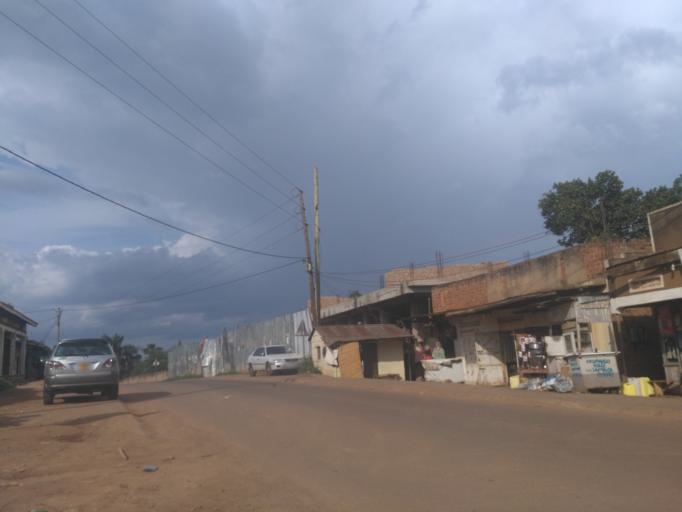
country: UG
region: Central Region
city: Kampala Central Division
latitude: 0.3567
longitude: 32.5827
